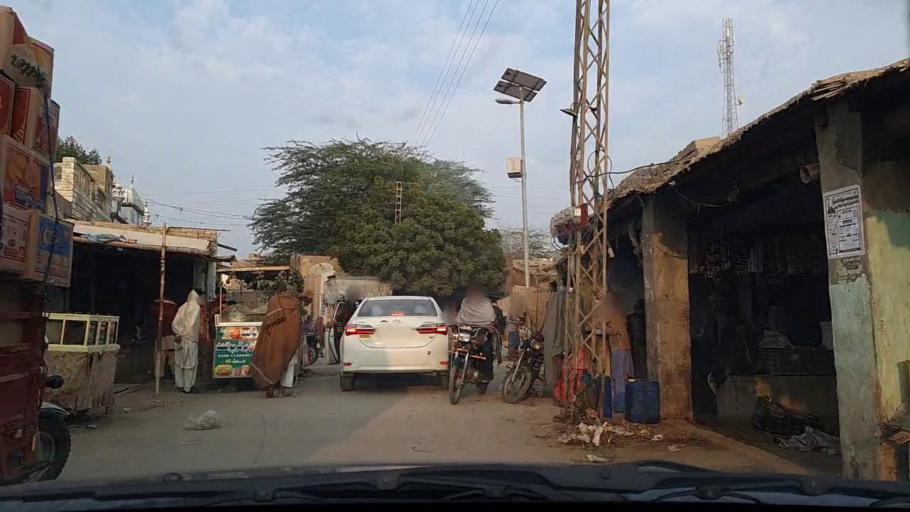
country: PK
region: Sindh
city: Pithoro
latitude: 25.6260
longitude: 69.4203
